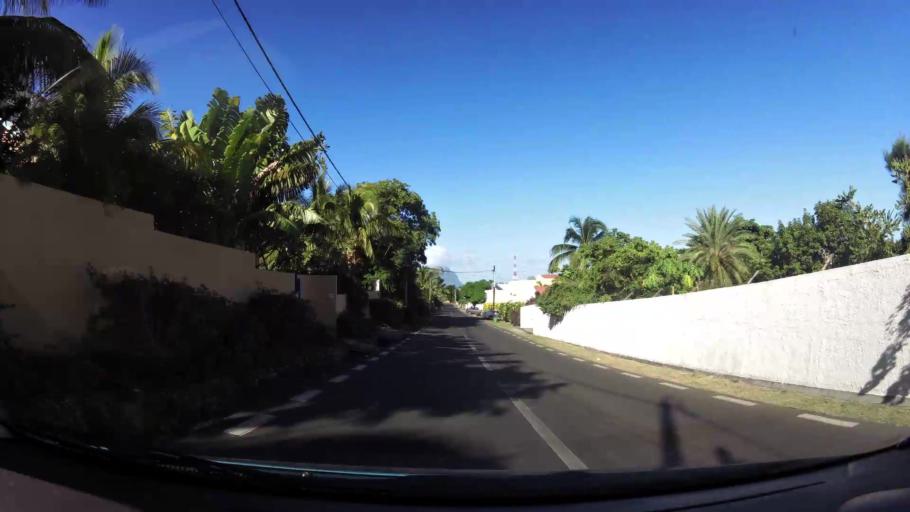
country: MU
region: Black River
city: Grande Riviere Noire
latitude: -20.3468
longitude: 57.3663
